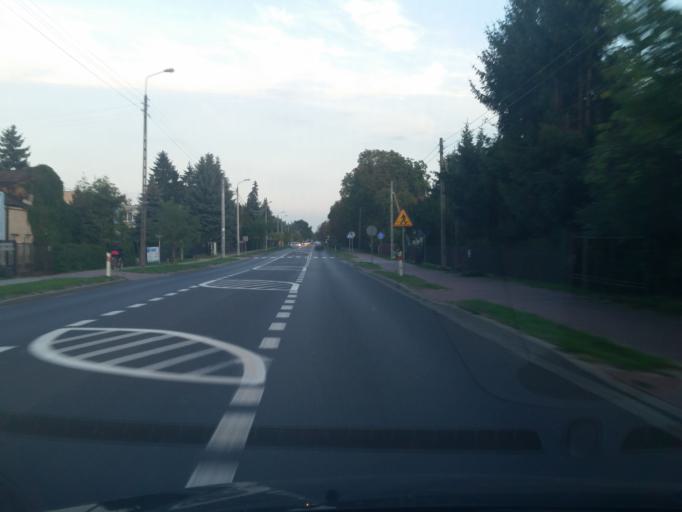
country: PL
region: Masovian Voivodeship
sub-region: Powiat legionowski
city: Jablonna
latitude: 52.3812
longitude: 20.9087
